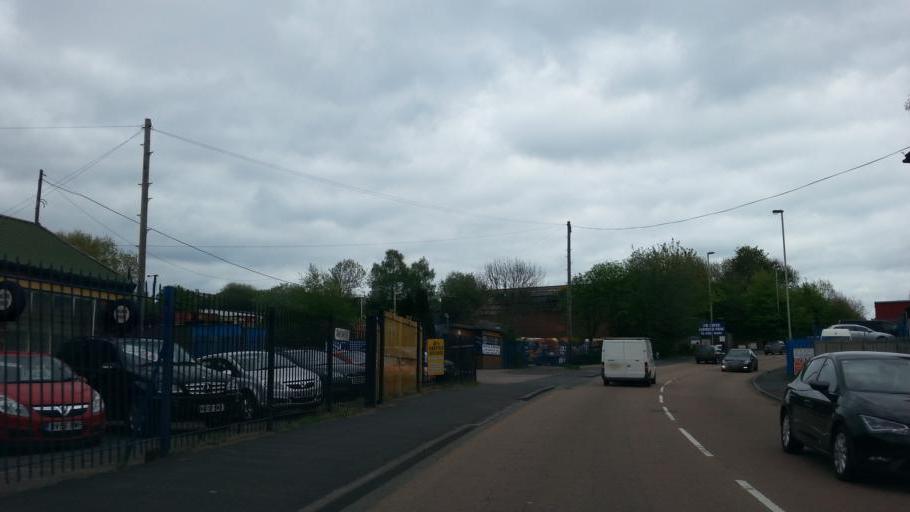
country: GB
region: England
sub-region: Dudley
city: Brierley Hill
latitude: 52.4583
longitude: -2.1068
